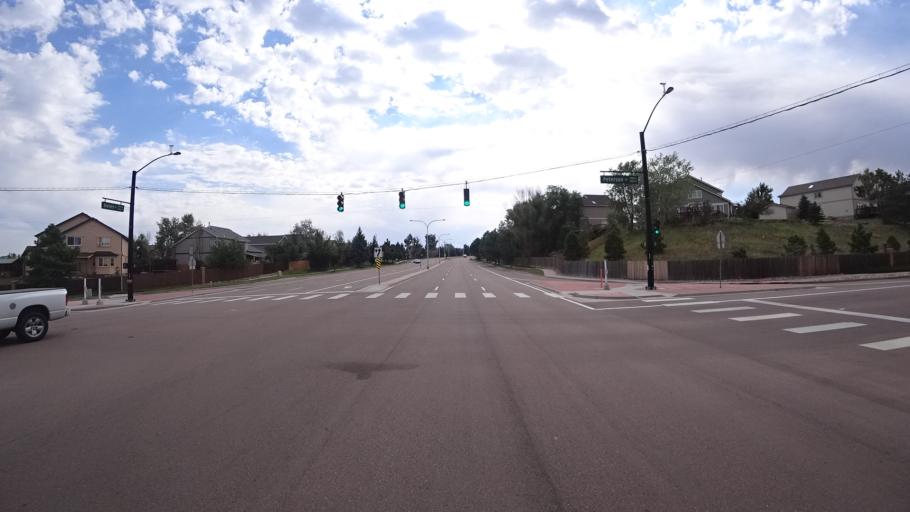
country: US
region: Colorado
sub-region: El Paso County
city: Cimarron Hills
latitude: 38.9026
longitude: -104.6965
